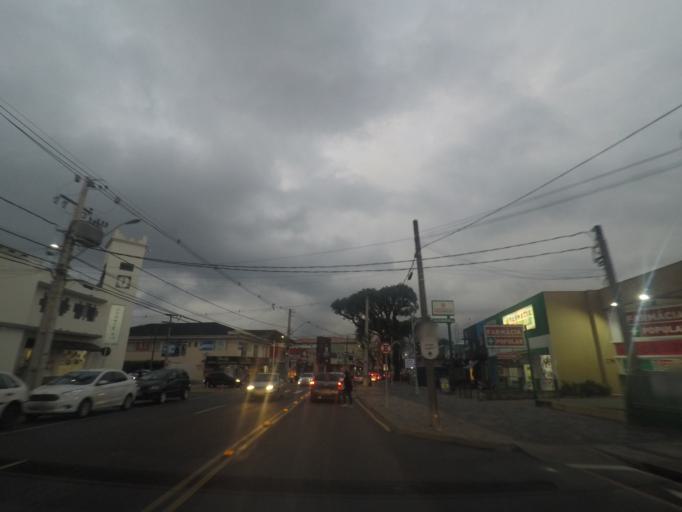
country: BR
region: Parana
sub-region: Curitiba
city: Curitiba
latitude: -25.4015
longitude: -49.3325
